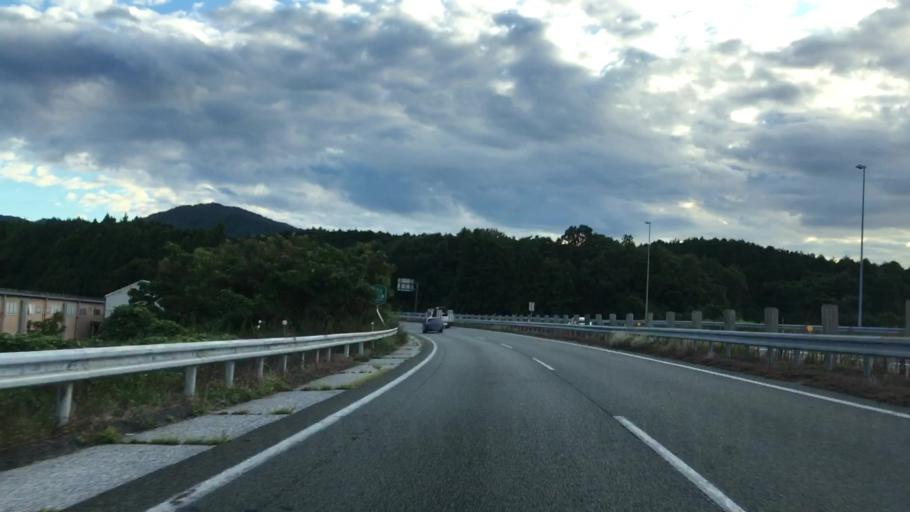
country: JP
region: Yamaguchi
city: Ogori-shimogo
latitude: 34.1697
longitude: 131.2432
